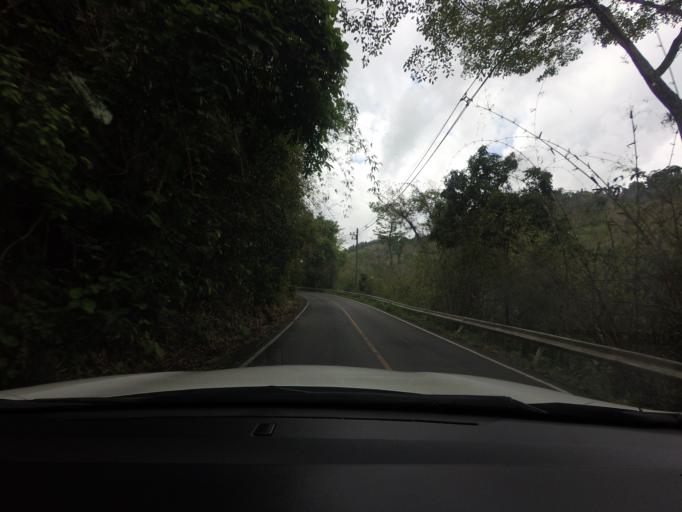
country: TH
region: Nakhon Ratchasima
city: Pak Chong
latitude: 14.4840
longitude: 101.3884
